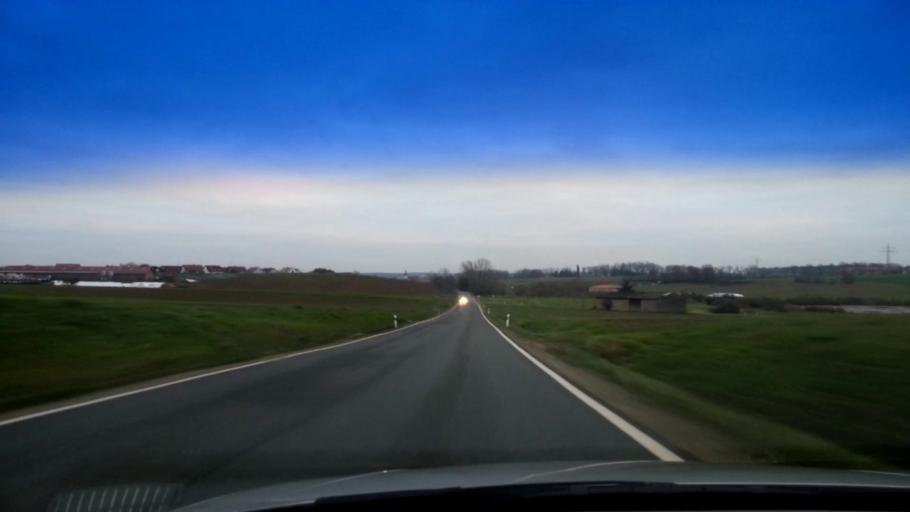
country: DE
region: Bavaria
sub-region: Upper Franconia
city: Pommersfelden
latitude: 49.7802
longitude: 10.7969
